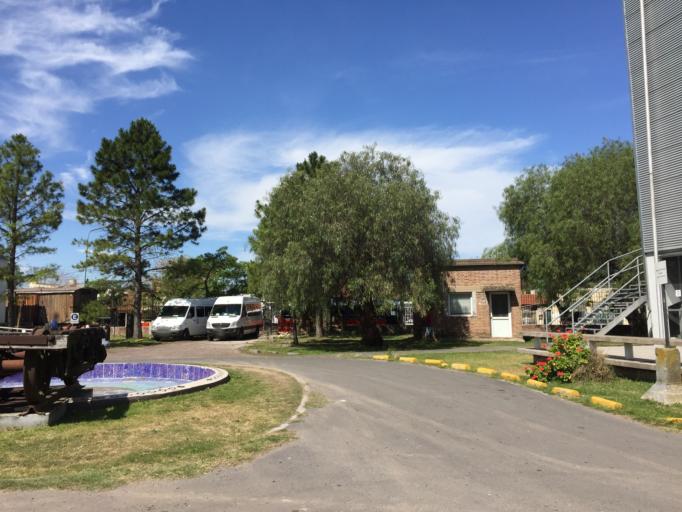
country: AR
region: Buenos Aires
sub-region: Partido de Lanus
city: Lanus
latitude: -34.7336
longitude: -58.3907
